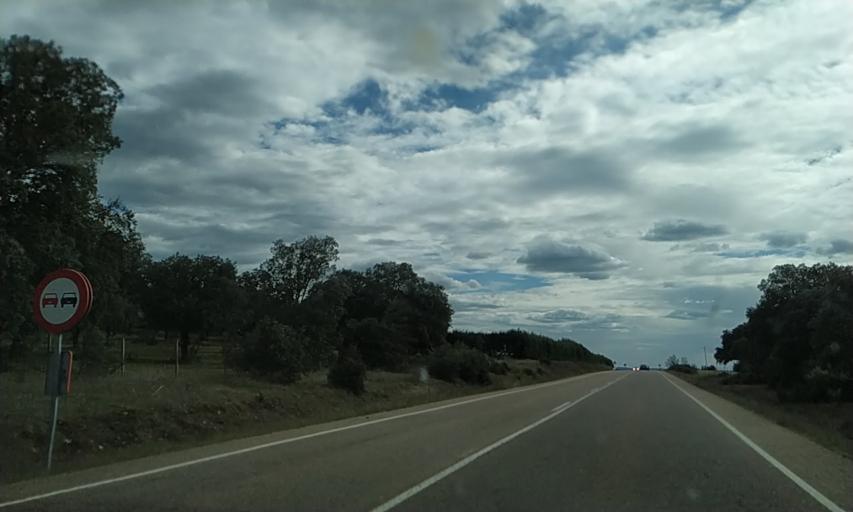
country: ES
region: Castille and Leon
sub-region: Provincia de Salamanca
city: Ciudad Rodrigo
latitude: 40.5702
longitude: -6.5450
